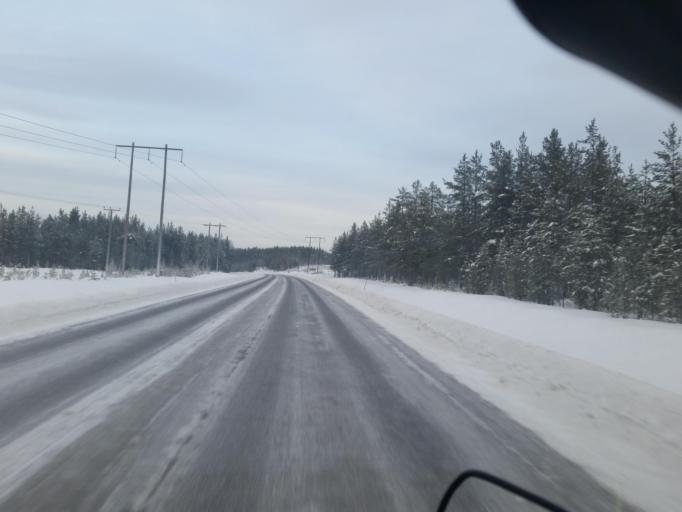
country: SE
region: Norrbotten
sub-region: Pitea Kommun
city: Pitea
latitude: 65.2583
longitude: 21.5385
